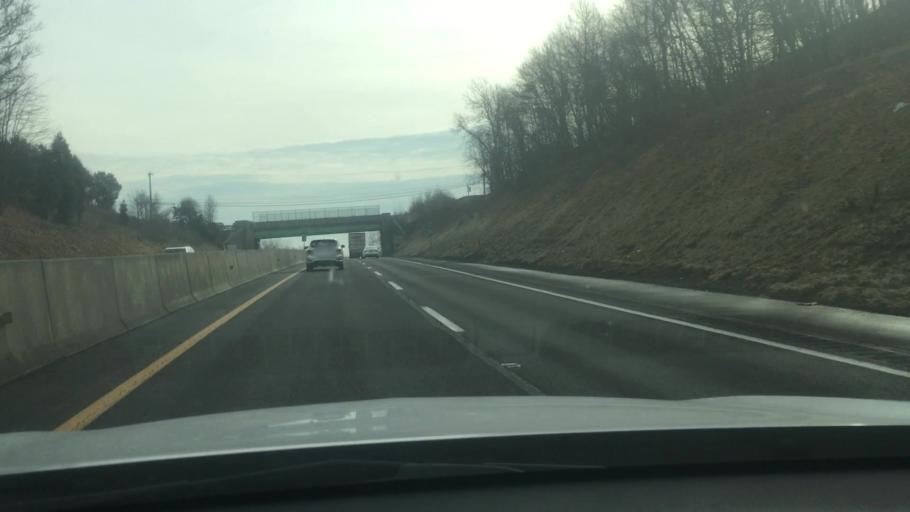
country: US
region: Pennsylvania
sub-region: Chester County
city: Elverson
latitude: 40.1497
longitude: -75.8382
